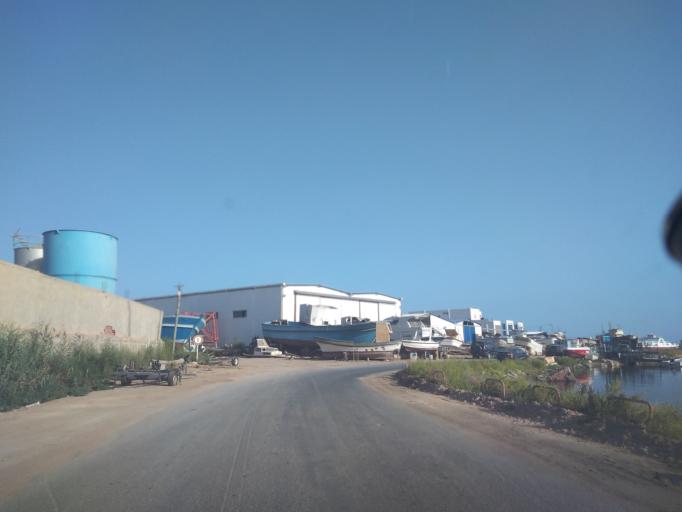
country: TN
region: Safaqis
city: Sfax
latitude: 34.7203
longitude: 10.7672
